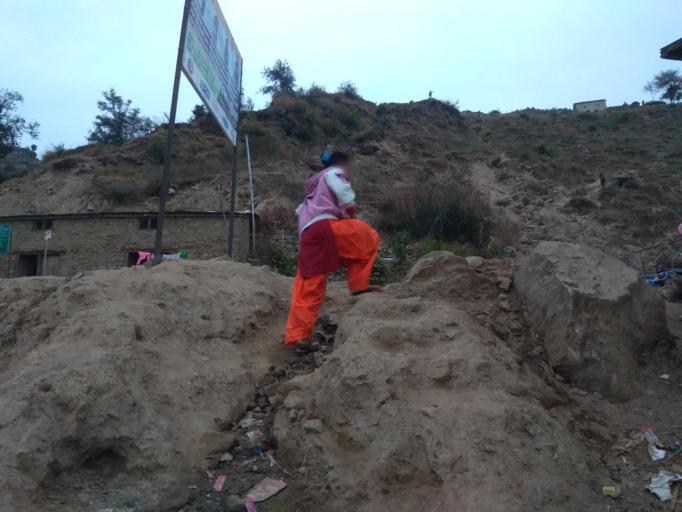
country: NP
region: Far Western
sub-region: Seti Zone
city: Achham
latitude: 29.2591
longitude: 81.6201
